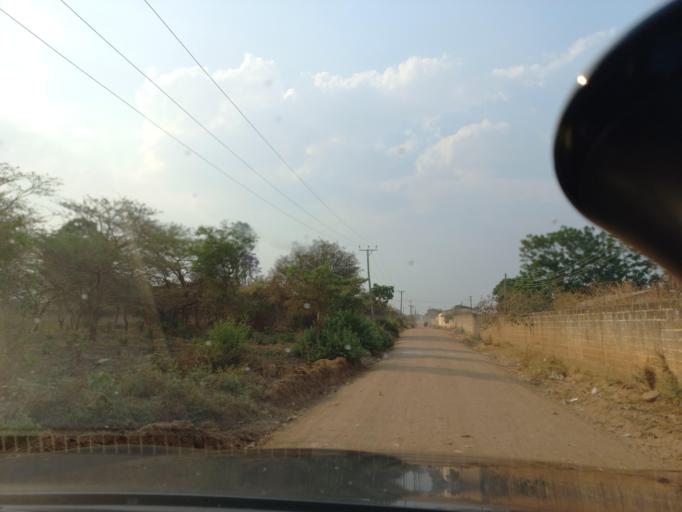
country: ZM
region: Lusaka
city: Lusaka
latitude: -15.4775
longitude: 28.2045
